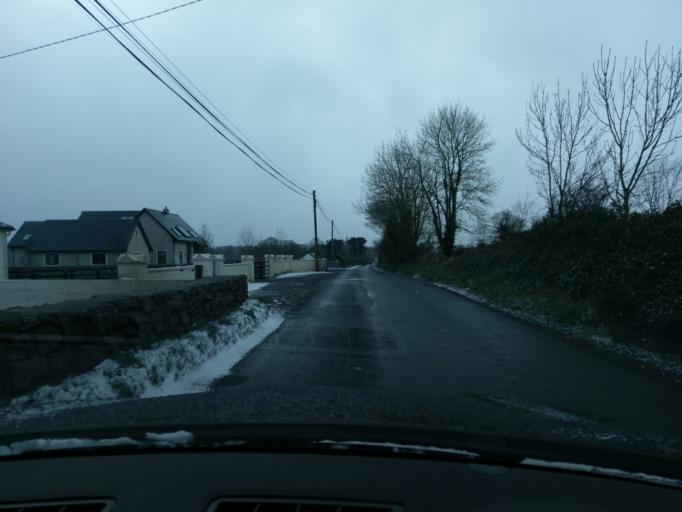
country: IE
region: Connaught
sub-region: County Galway
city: Oranmore
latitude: 53.2467
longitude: -8.8508
